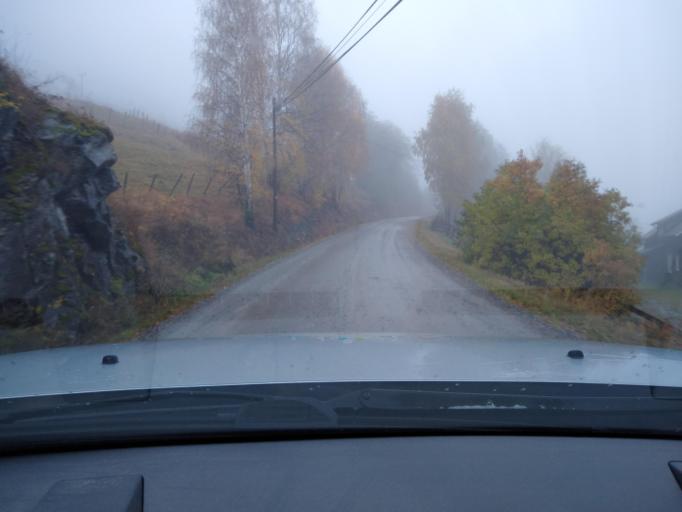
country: NO
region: Oppland
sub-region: Ringebu
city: Ringebu
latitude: 61.5292
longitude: 10.1561
